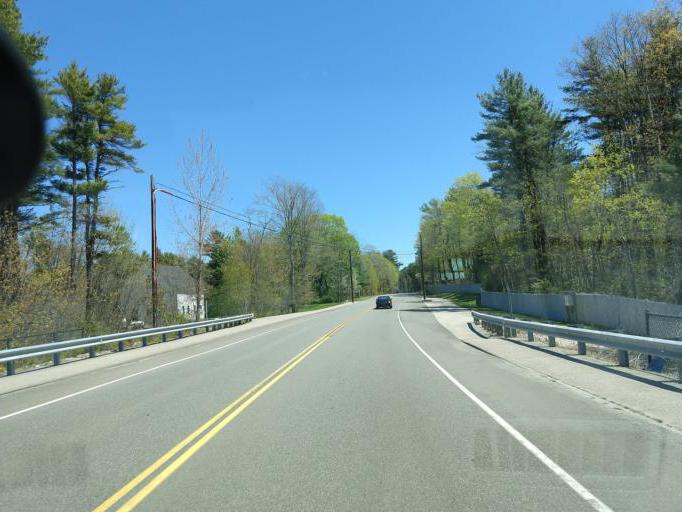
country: US
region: Maine
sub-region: York County
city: York Harbor
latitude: 43.1415
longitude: -70.6918
